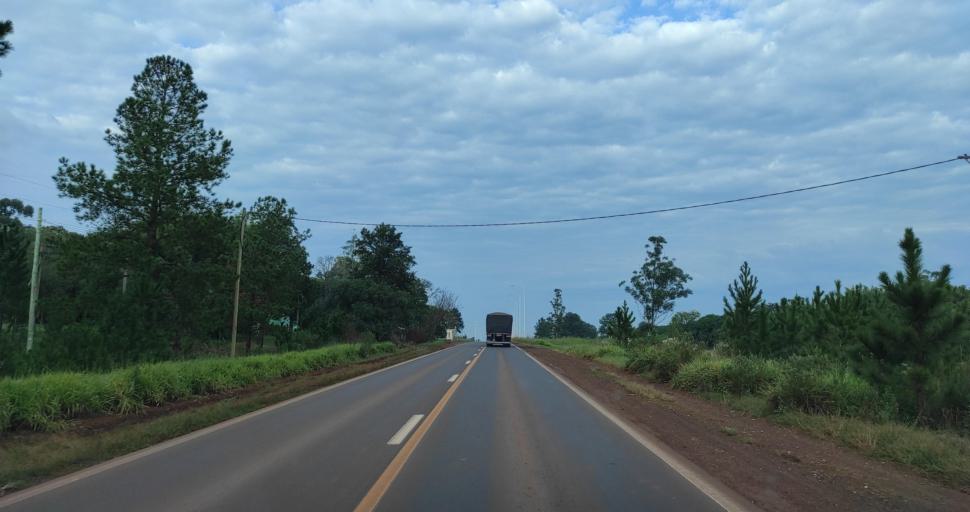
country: AR
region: Corrientes
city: Gobernador Ingeniero Valentin Virasoro
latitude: -27.9636
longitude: -56.0054
